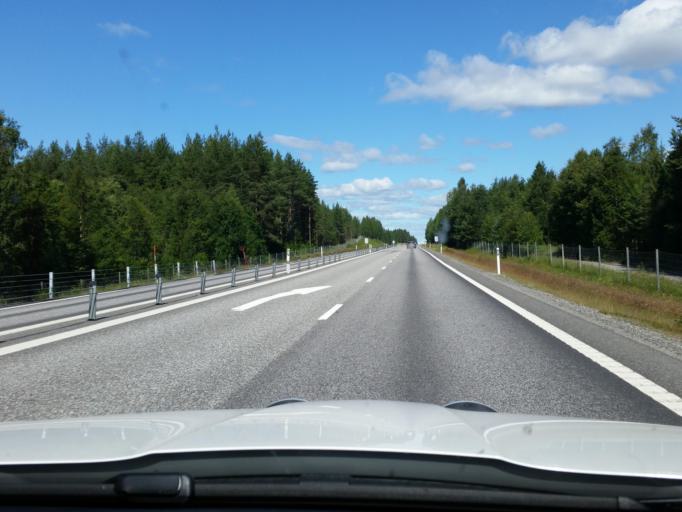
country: SE
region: Norrbotten
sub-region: Pitea Kommun
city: Pitea
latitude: 65.2631
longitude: 21.4638
